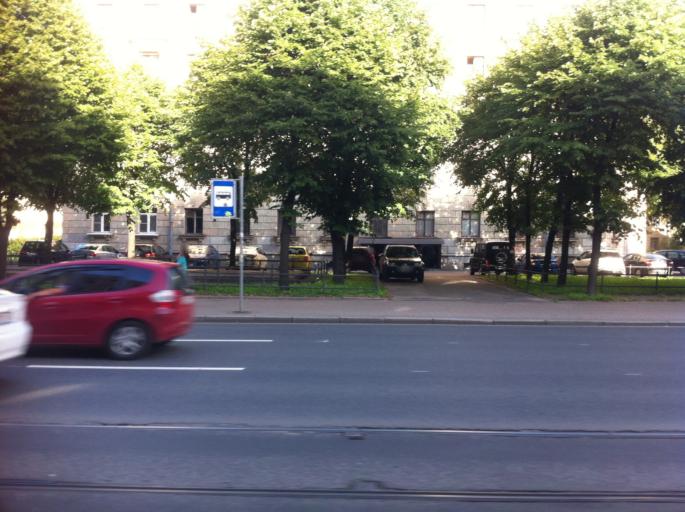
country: RU
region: St.-Petersburg
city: Admiralteisky
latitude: 59.9121
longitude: 30.2768
